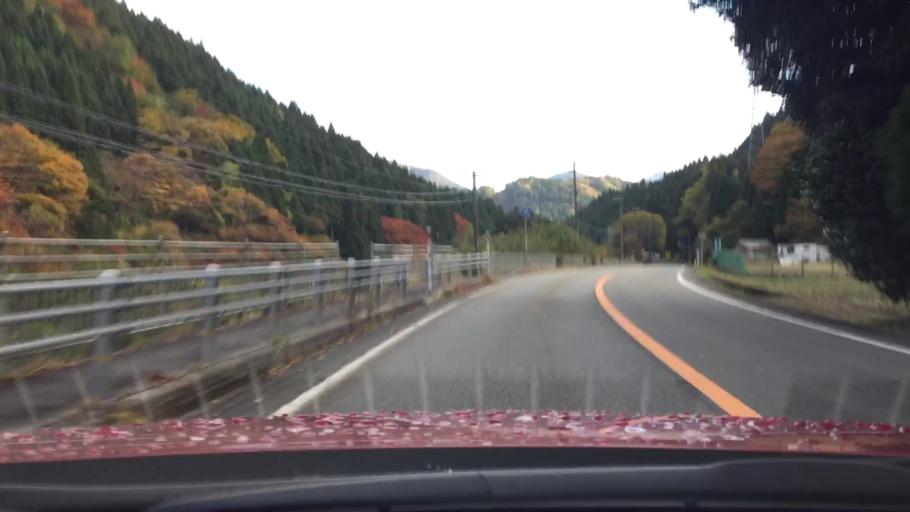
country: JP
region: Hyogo
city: Yamazakicho-nakabirose
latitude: 35.1848
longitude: 134.5341
